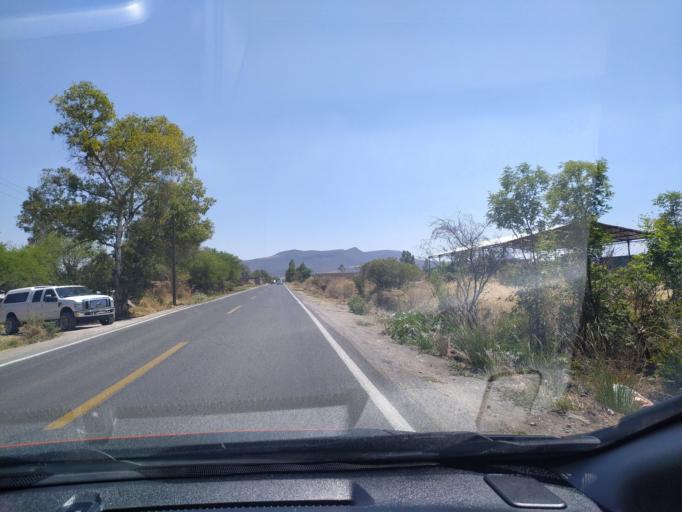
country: MX
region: Guanajuato
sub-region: San Francisco del Rincon
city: San Ignacio de Hidalgo
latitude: 20.8550
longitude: -101.8581
